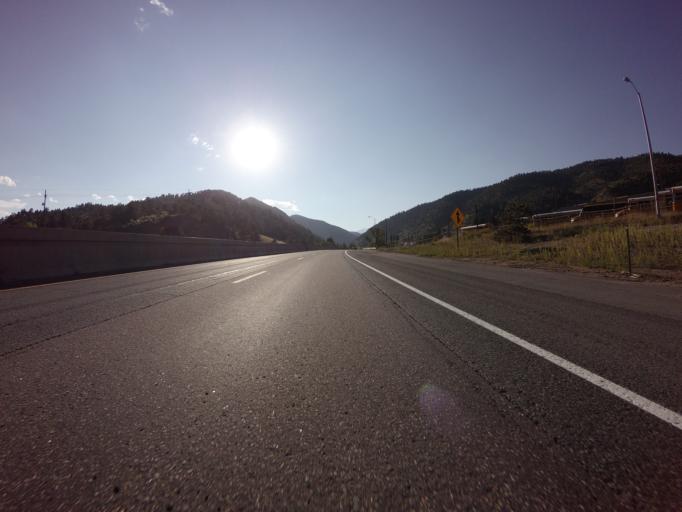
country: US
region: Colorado
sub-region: Clear Creek County
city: Idaho Springs
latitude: 39.7411
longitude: -105.5211
